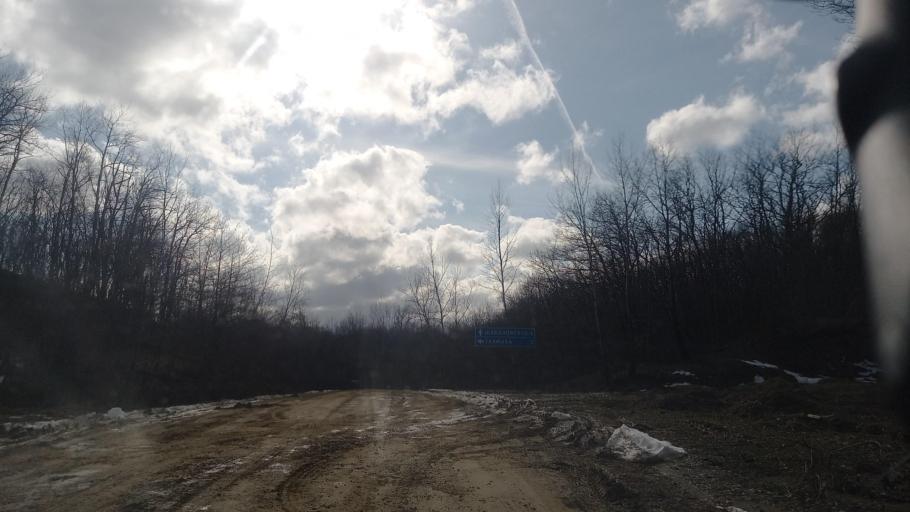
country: RU
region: Krasnodarskiy
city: Smolenskaya
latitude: 44.5980
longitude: 38.8319
